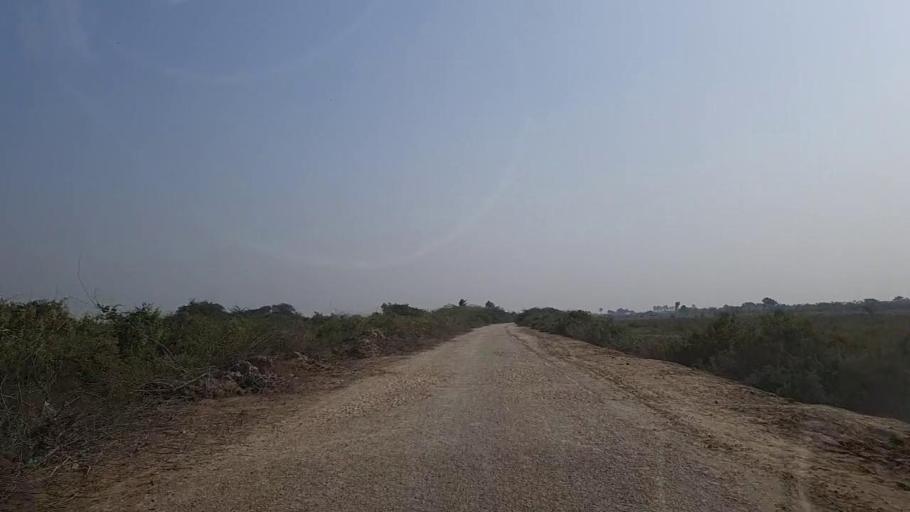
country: PK
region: Sindh
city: Keti Bandar
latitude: 24.2512
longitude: 67.6289
